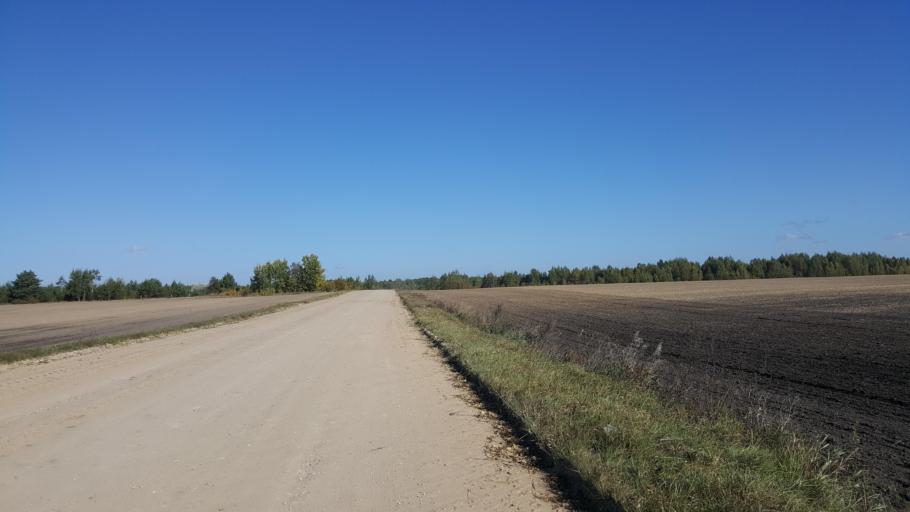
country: BY
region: Brest
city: Kamyanyets
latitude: 52.4312
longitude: 23.8830
